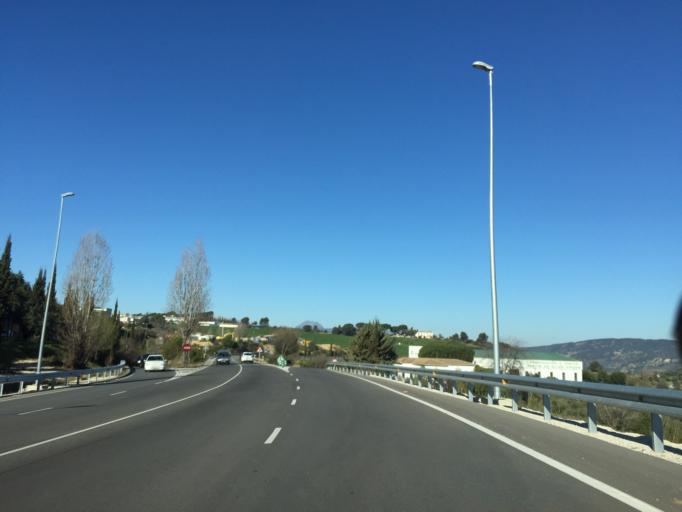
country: ES
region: Andalusia
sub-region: Provincia de Malaga
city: Ronda
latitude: 36.7551
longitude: -5.1507
